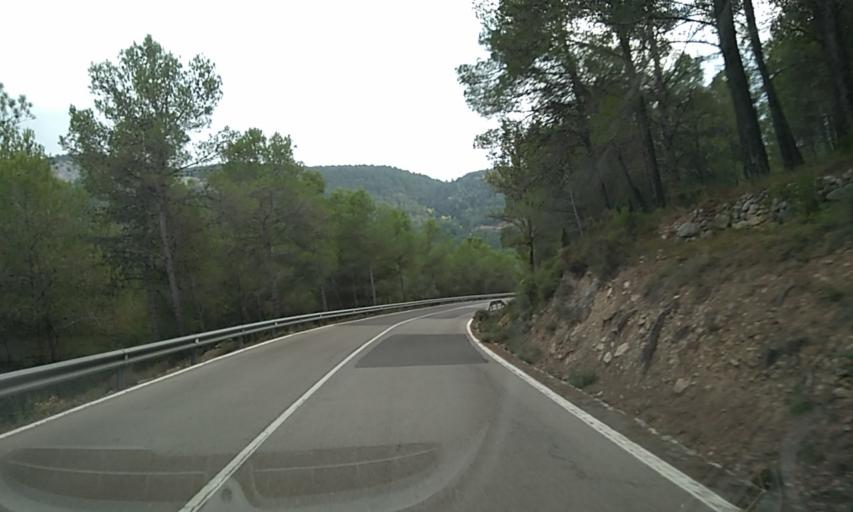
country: ES
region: Valencia
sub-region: Provincia de Castello
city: Puebla de Arenoso
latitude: 40.0914
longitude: -0.5662
